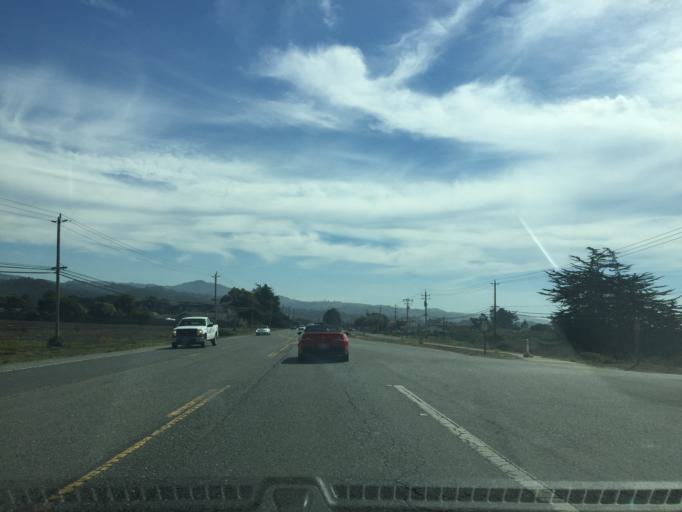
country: US
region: California
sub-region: San Mateo County
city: Half Moon Bay
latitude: 37.4815
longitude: -122.4450
